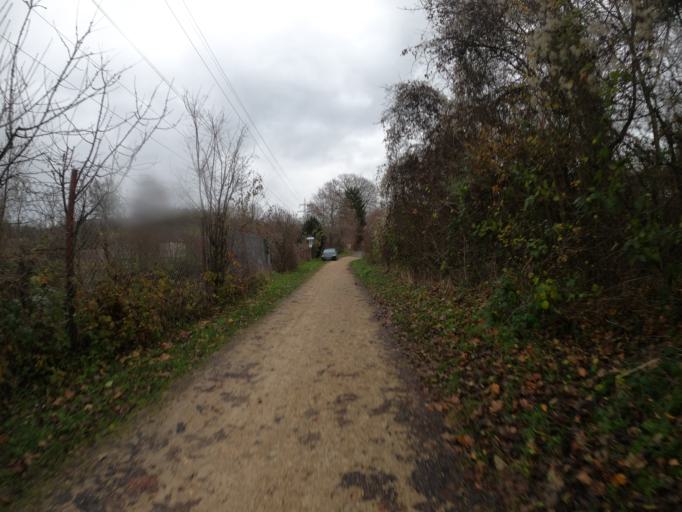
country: DE
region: Baden-Wuerttemberg
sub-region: Regierungsbezirk Stuttgart
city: Sussen
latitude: 48.6854
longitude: 9.7486
